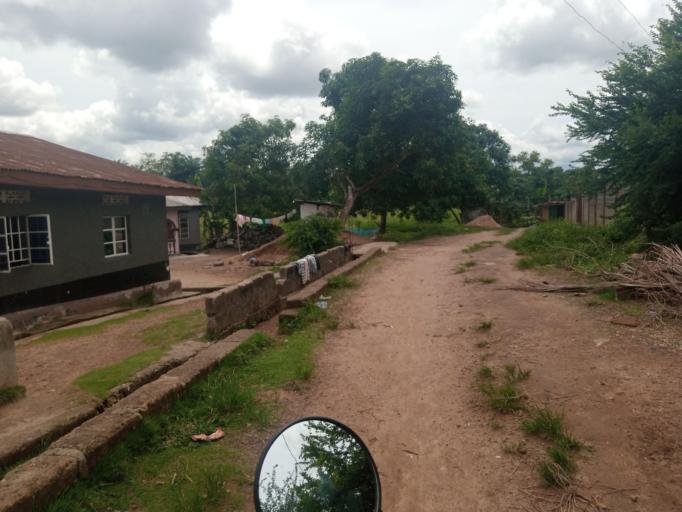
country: SL
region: Southern Province
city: Bo
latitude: 7.9563
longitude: -11.7183
